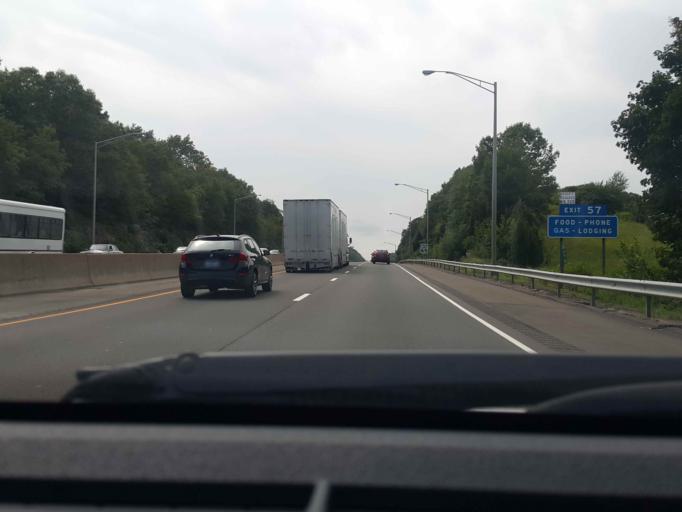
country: US
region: Connecticut
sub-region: New Haven County
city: Guilford
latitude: 41.2962
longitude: -72.6949
